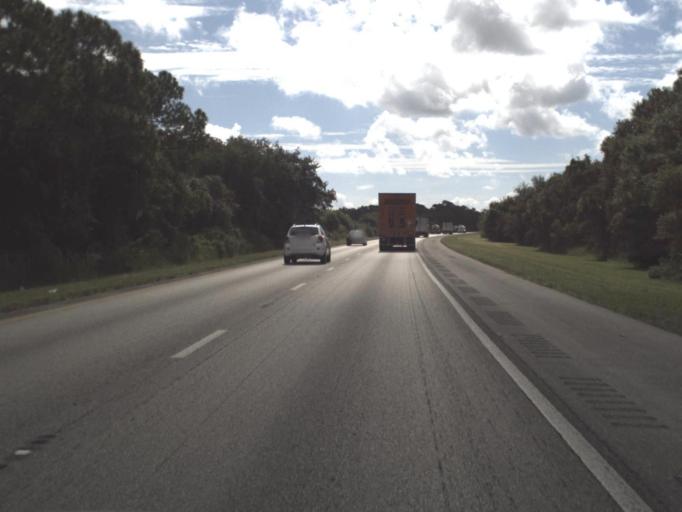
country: US
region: Florida
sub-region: Sarasota County
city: North Port
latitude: 27.0965
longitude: -82.1292
